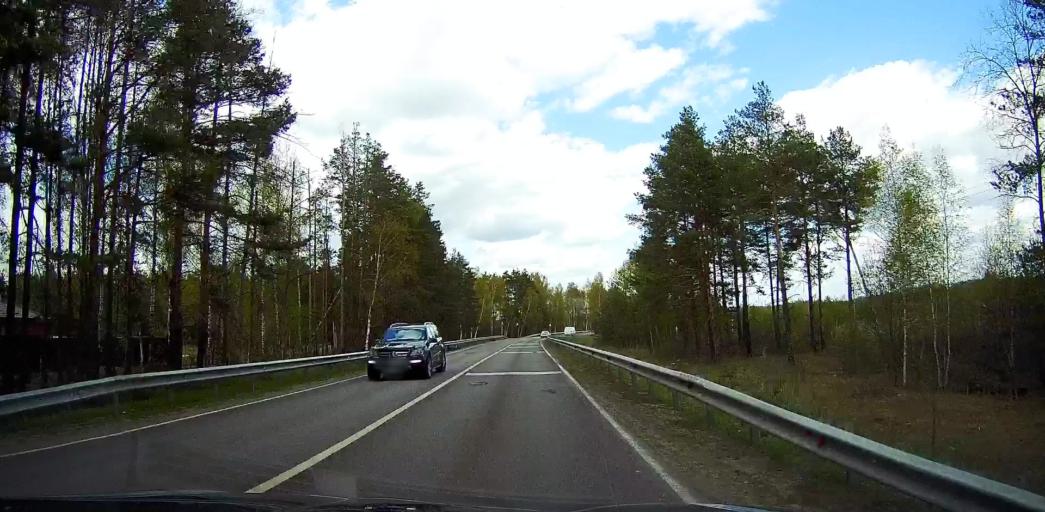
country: RU
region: Moskovskaya
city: Davydovo
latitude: 55.6282
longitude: 38.8621
